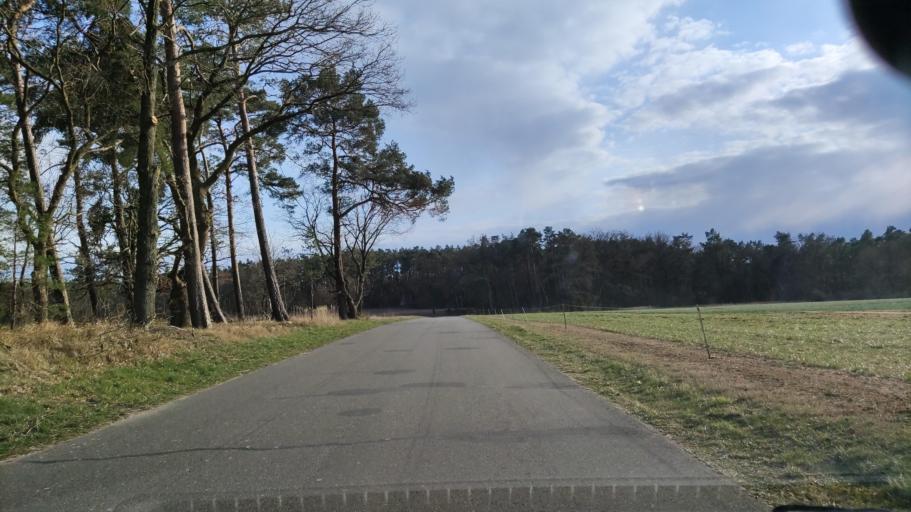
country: DE
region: Lower Saxony
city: Klein Gusborn
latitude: 53.0844
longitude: 11.2216
